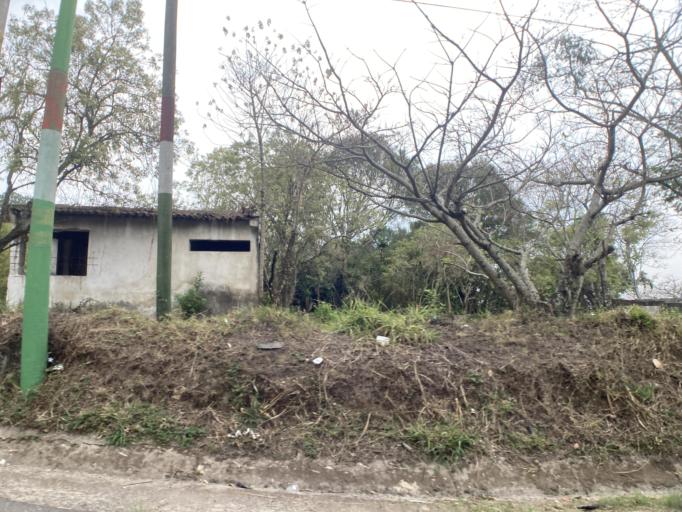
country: GT
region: Guatemala
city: Fraijanes
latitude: 14.4393
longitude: -90.4760
